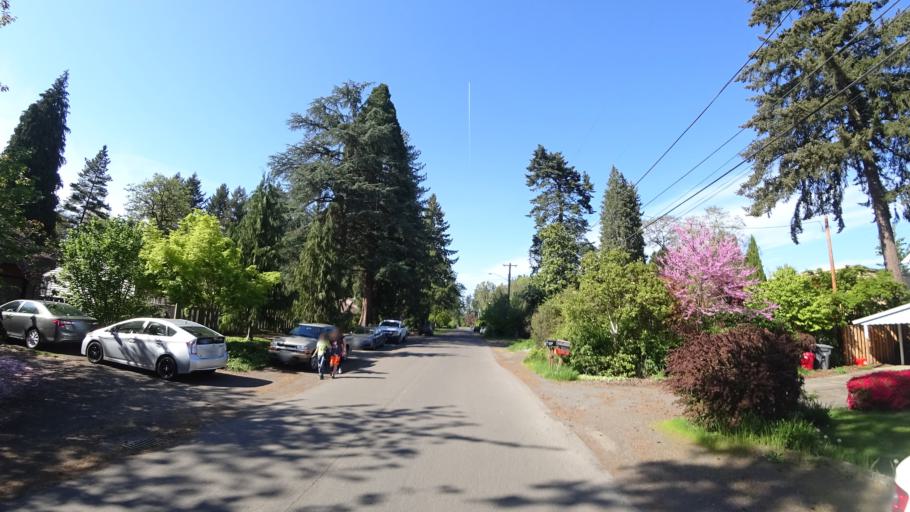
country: US
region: Oregon
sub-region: Washington County
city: Hillsboro
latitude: 45.5305
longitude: -122.9859
